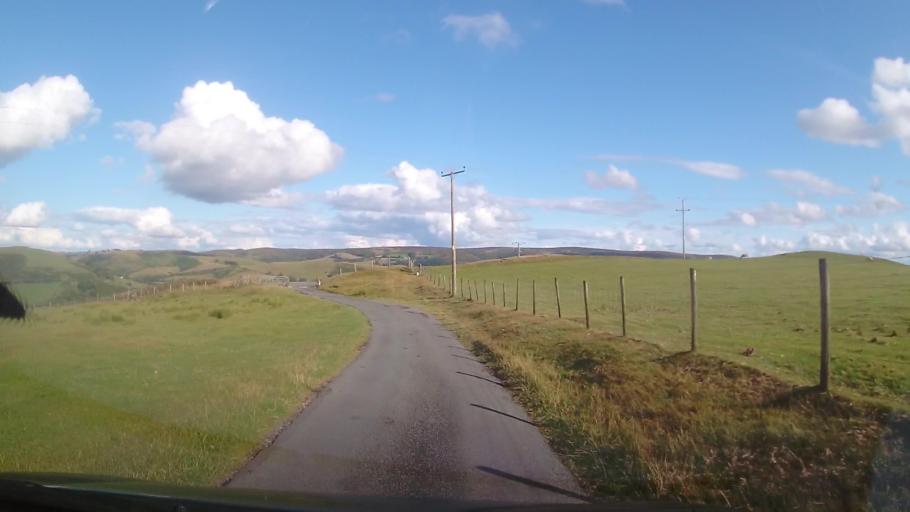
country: GB
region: England
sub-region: Shropshire
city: Norbury
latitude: 52.5717
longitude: -2.9179
